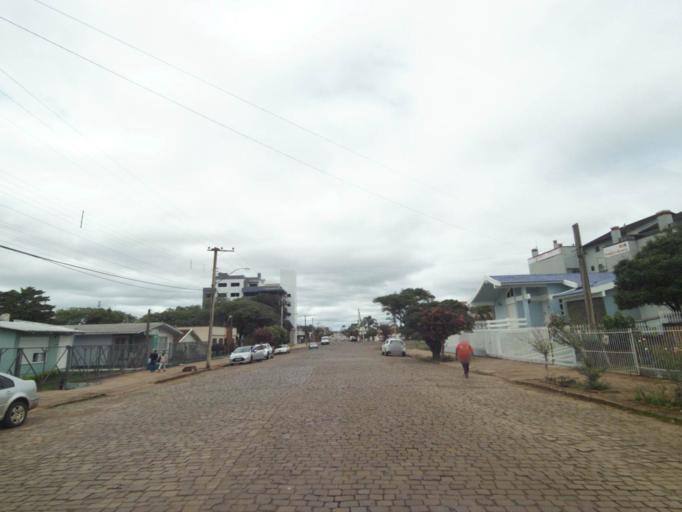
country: BR
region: Rio Grande do Sul
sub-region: Lagoa Vermelha
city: Lagoa Vermelha
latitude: -28.2116
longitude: -51.5171
